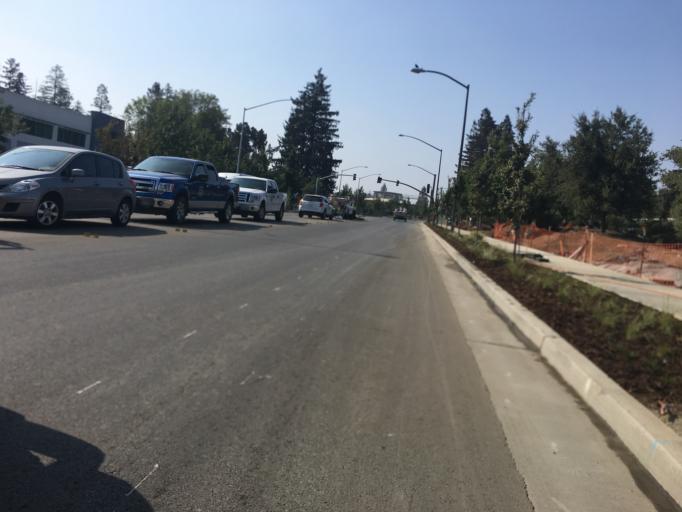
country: US
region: California
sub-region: Santa Clara County
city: Cupertino
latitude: 37.3354
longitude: -122.0055
